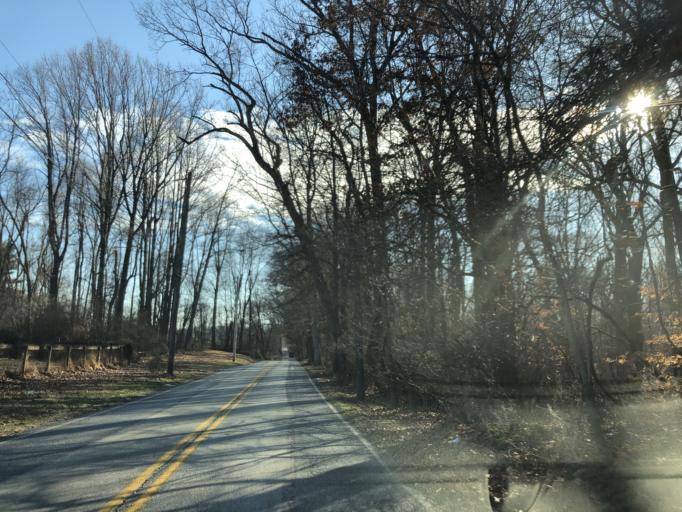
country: US
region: Pennsylvania
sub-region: Chester County
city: Upland
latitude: 39.8784
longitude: -75.7740
